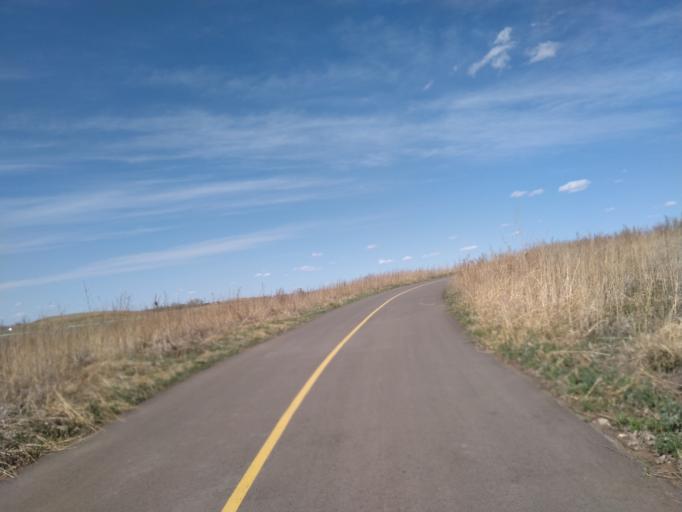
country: CA
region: Alberta
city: Chestermere
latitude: 51.0160
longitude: -113.9314
